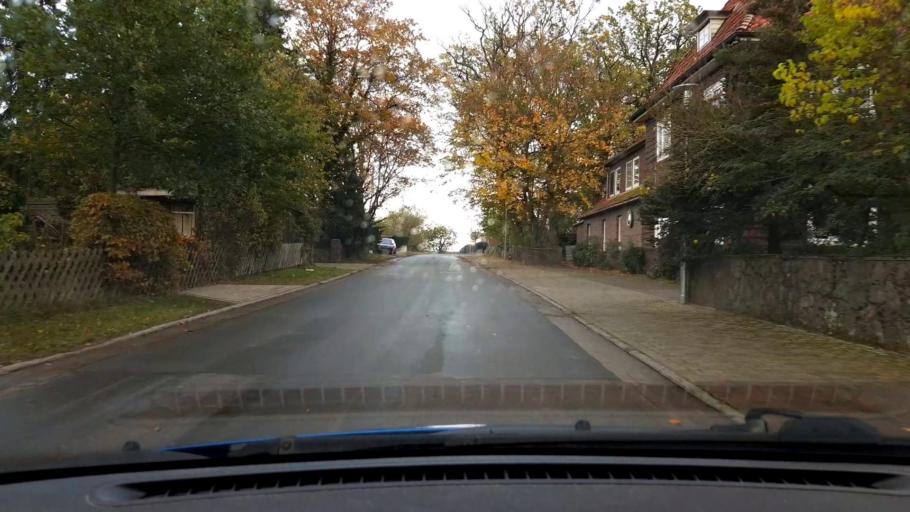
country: DE
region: Lower Saxony
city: Reinstorf
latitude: 53.2507
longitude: 10.5672
